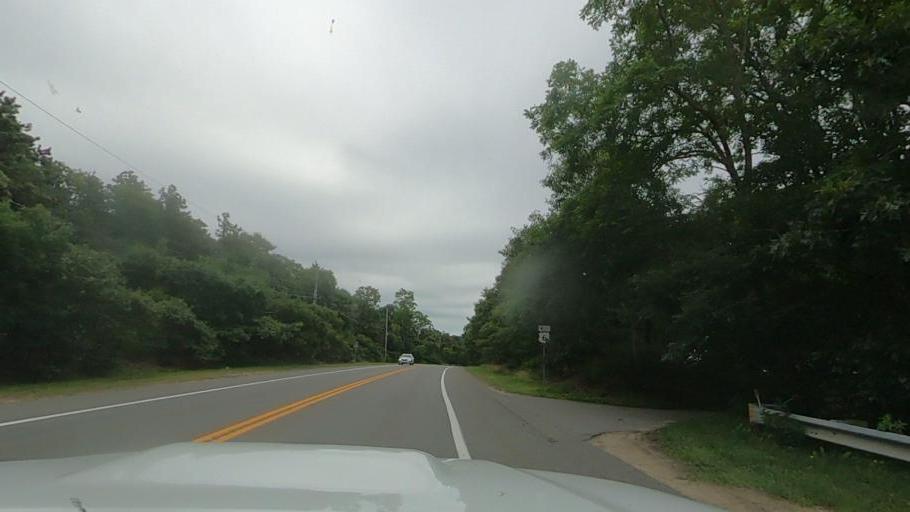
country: US
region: Massachusetts
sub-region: Barnstable County
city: Truro
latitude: 41.9993
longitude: -70.0496
